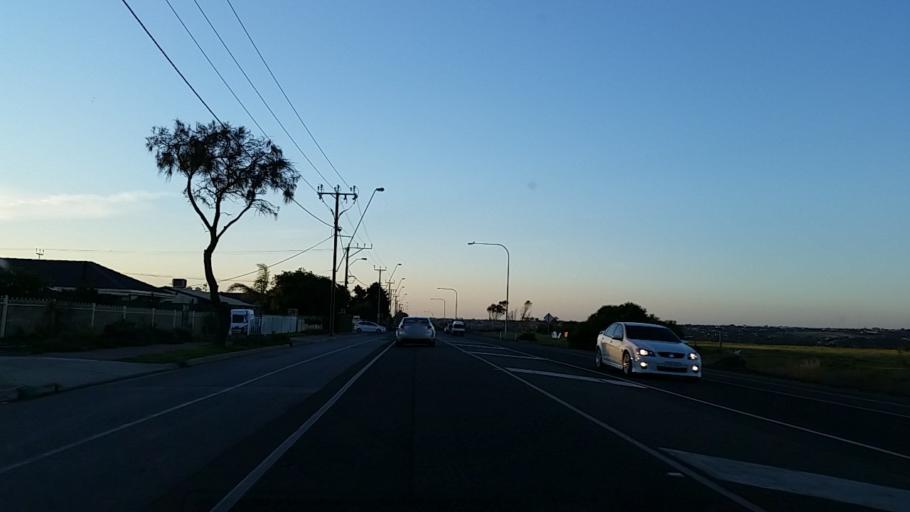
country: AU
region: South Australia
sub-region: Onkaparinga
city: Seaford
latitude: -35.1703
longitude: 138.4759
